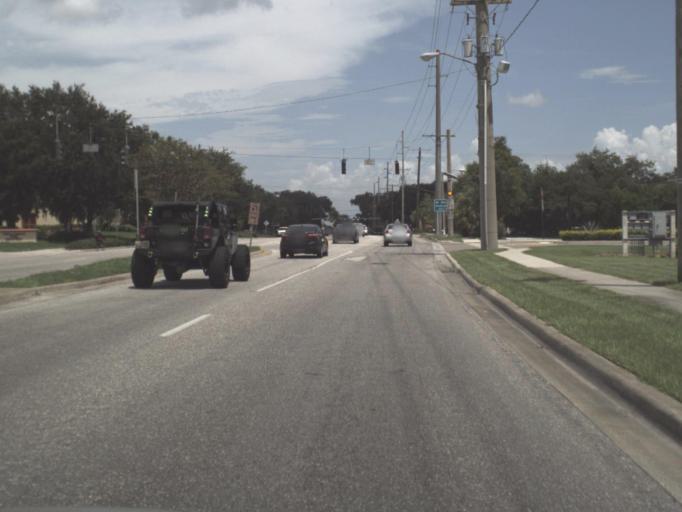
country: US
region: Florida
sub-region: Hillsborough County
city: Temple Terrace
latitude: 28.0325
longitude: -82.3929
